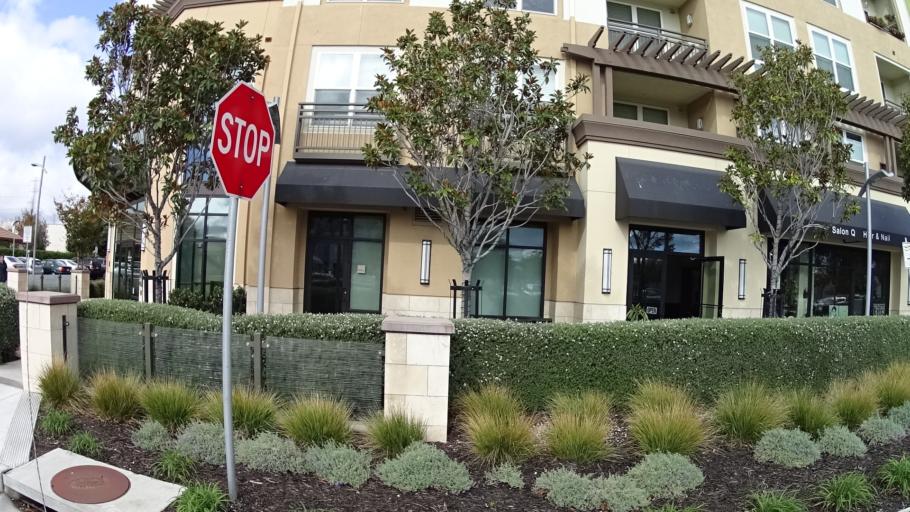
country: US
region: California
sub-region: San Mateo County
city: Foster City
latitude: 37.5640
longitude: -122.2703
